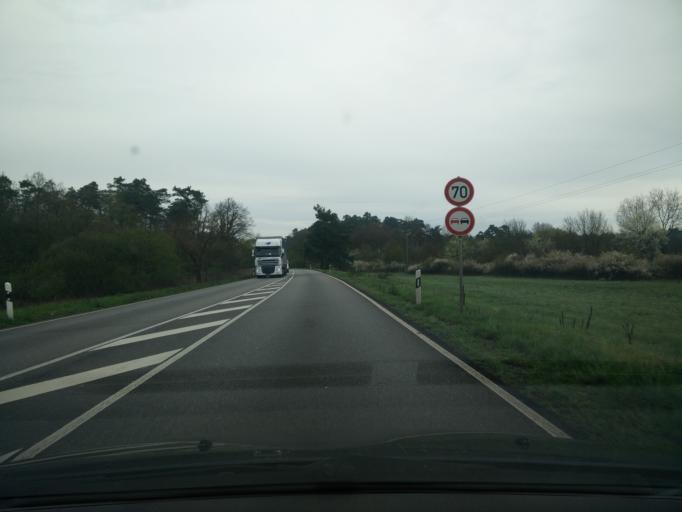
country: DE
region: Rheinland-Pfalz
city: Kandel
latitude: 49.0551
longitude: 8.2019
